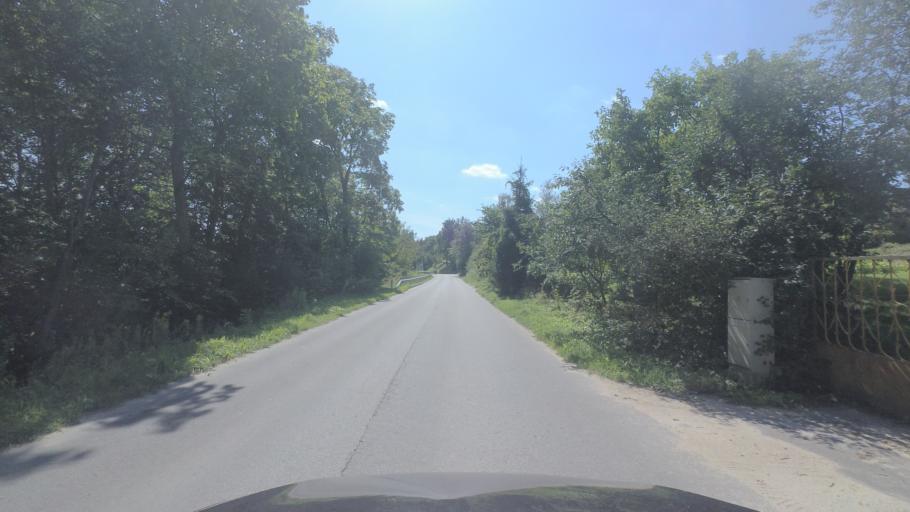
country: LT
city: Nemencine
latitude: 54.8511
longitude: 25.3744
